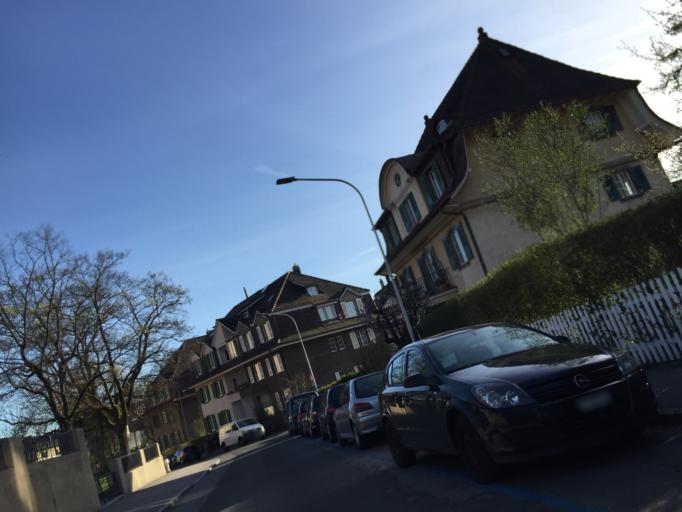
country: CH
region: Bern
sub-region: Bern-Mittelland District
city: Koniz
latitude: 46.9418
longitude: 7.4215
